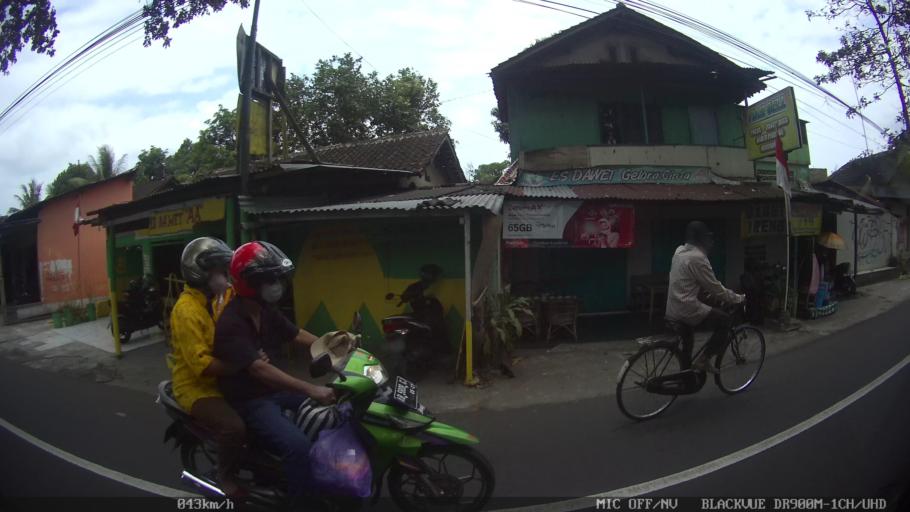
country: ID
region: Central Java
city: Candi Prambanan
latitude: -7.7571
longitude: 110.4813
